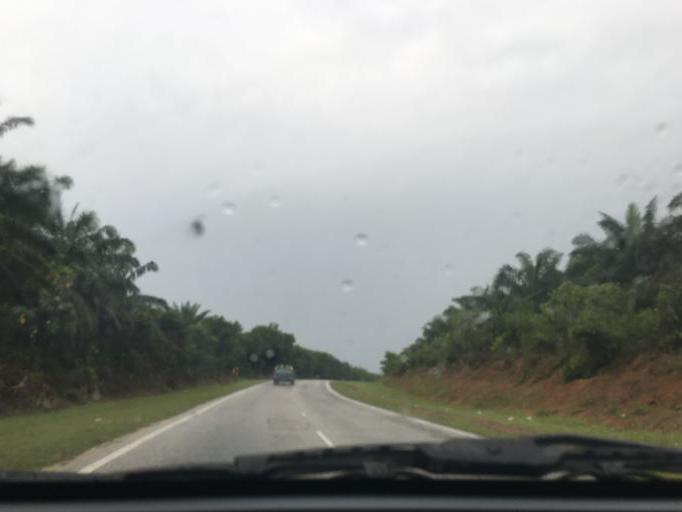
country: MY
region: Kedah
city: Sungai Petani
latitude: 5.6221
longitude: 100.6380
